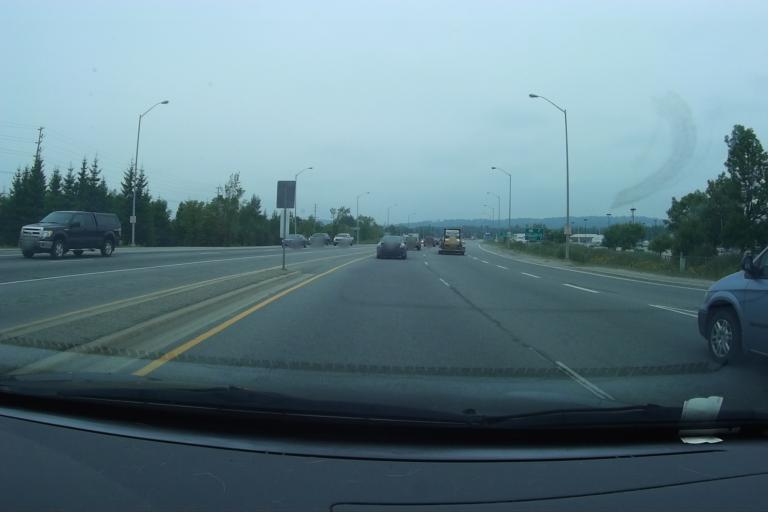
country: CA
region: Ontario
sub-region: Nipissing District
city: North Bay
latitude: 46.3130
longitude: -79.4434
